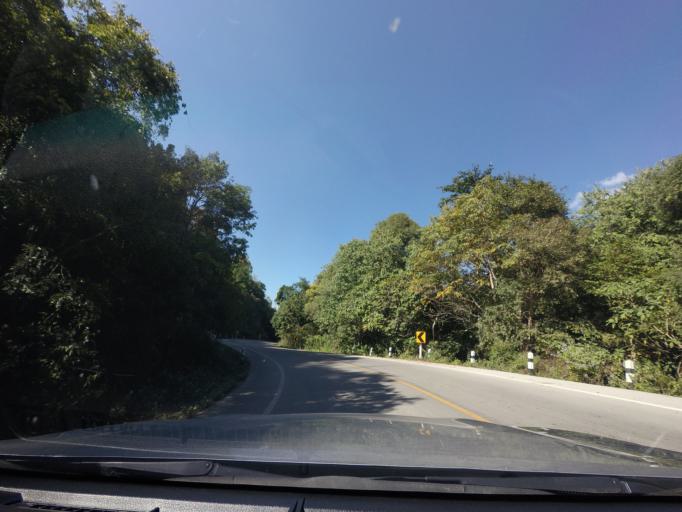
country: TH
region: Lampang
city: Chae Hom
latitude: 18.6366
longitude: 99.6098
